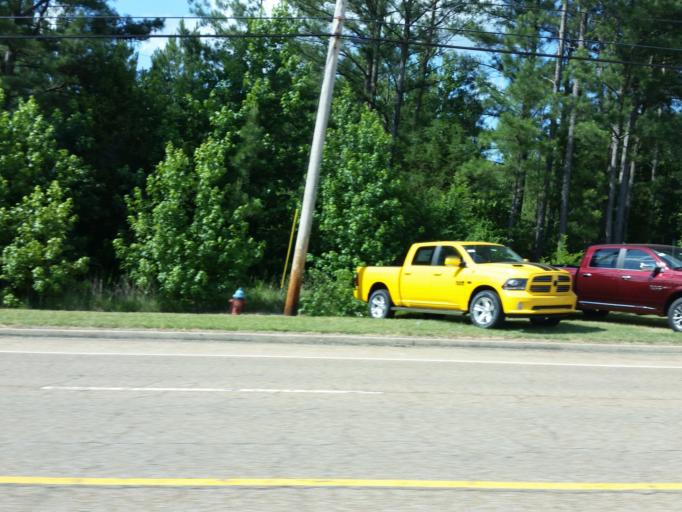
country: US
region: Tennessee
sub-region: Henderson County
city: Lexington
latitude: 35.6419
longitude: -88.3805
